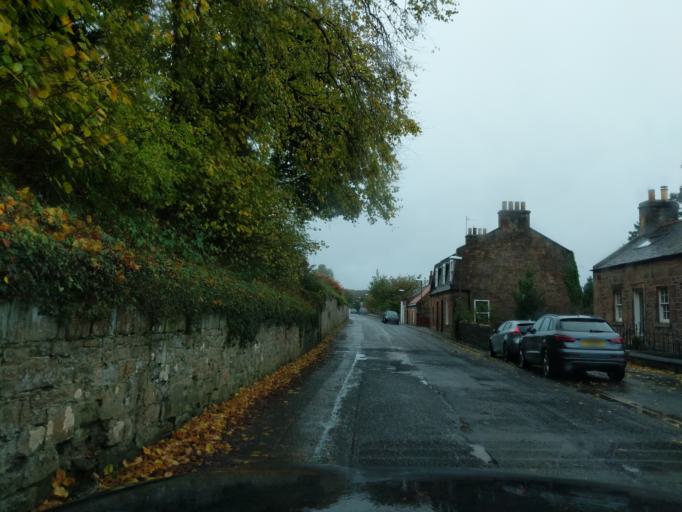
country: GB
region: Scotland
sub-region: East Lothian
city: Dunbar
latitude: 55.9572
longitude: -2.4471
